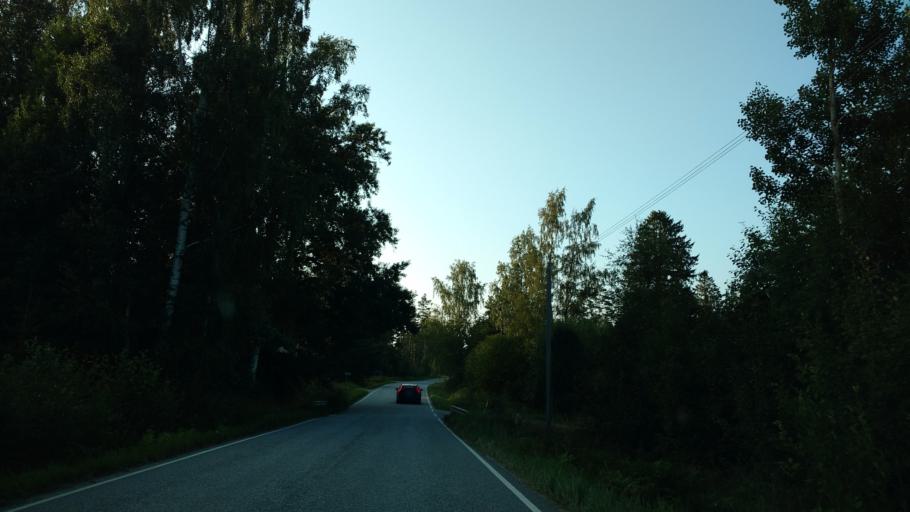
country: FI
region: Varsinais-Suomi
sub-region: Aboland-Turunmaa
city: Dragsfjaerd
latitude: 60.0643
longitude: 22.4517
